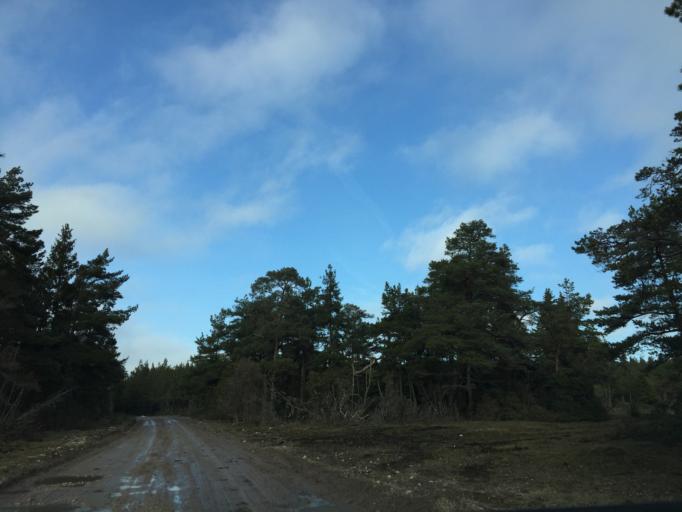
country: EE
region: Saare
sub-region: Kuressaare linn
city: Kuressaare
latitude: 58.4831
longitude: 21.9460
